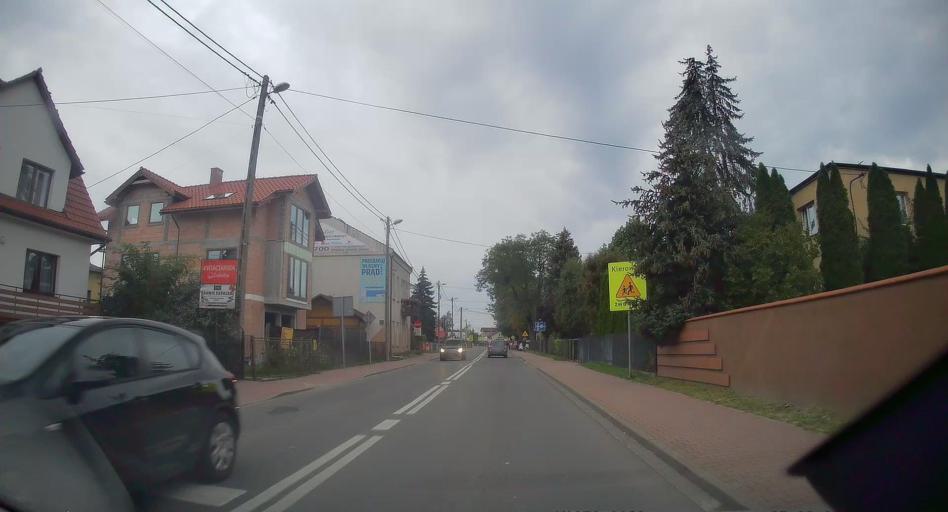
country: PL
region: Lesser Poland Voivodeship
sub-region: Powiat wielicki
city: Niepolomice
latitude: 50.0328
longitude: 20.2135
